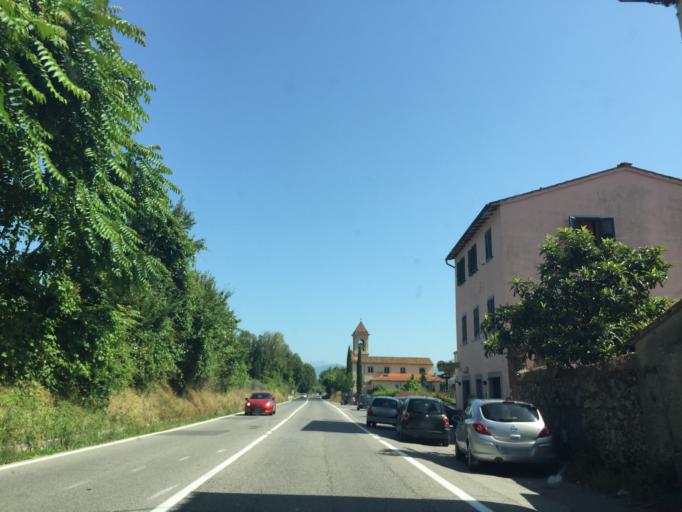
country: IT
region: Tuscany
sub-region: Provincia di Lucca
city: Lucca
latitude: 43.8095
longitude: 10.4855
